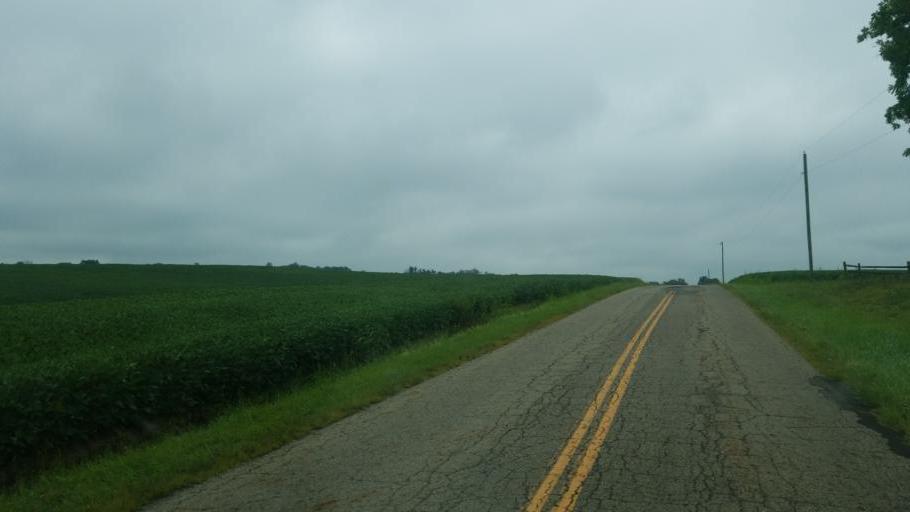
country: US
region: Ohio
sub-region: Licking County
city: Utica
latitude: 40.2579
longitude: -82.4133
